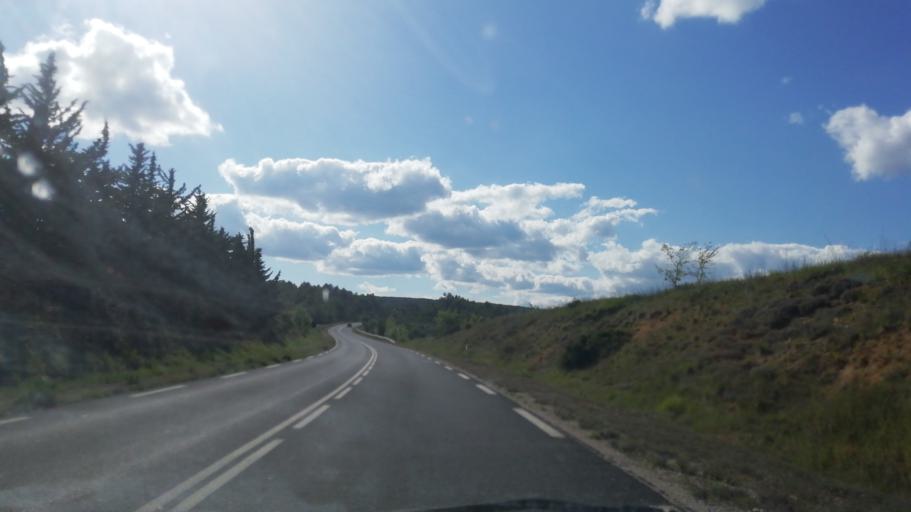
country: FR
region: Languedoc-Roussillon
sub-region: Departement de l'Herault
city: Saint-Gely-du-Fesc
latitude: 43.7085
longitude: 3.8062
